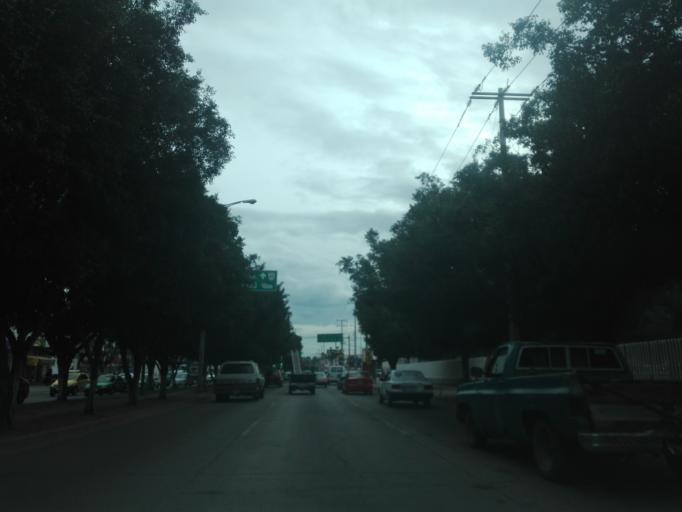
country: MX
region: Guanajuato
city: Leon
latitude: 21.1077
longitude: -101.6573
